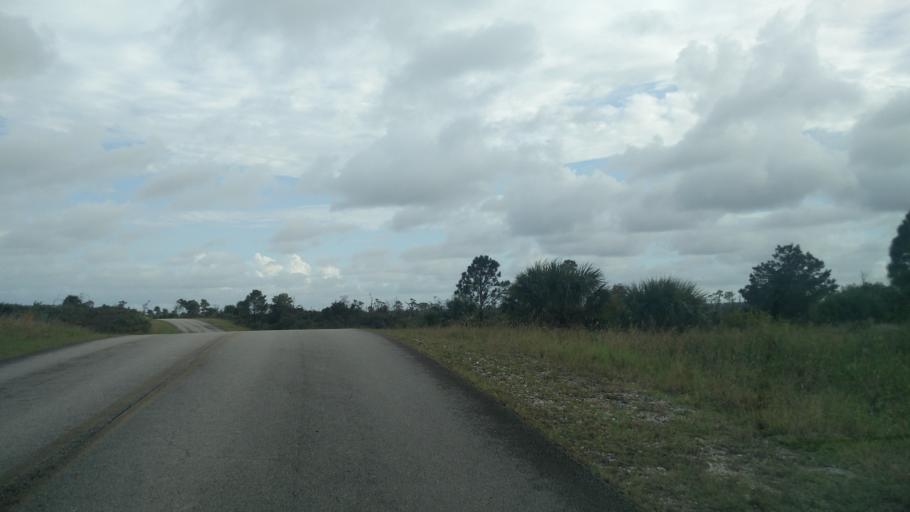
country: US
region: Florida
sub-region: Palm Beach County
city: Tequesta
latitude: 27.0106
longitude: -80.1094
